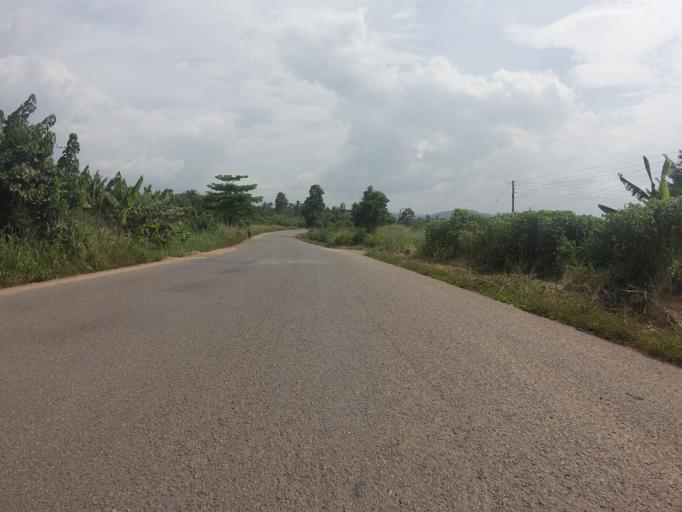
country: GH
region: Eastern
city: Koforidua
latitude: 5.9780
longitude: -0.2301
